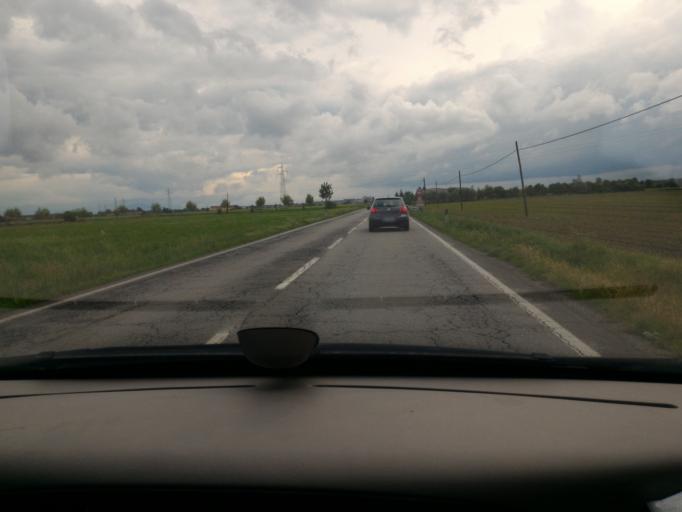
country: IT
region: Piedmont
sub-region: Provincia di Cuneo
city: Genola
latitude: 44.6136
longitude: 7.6631
